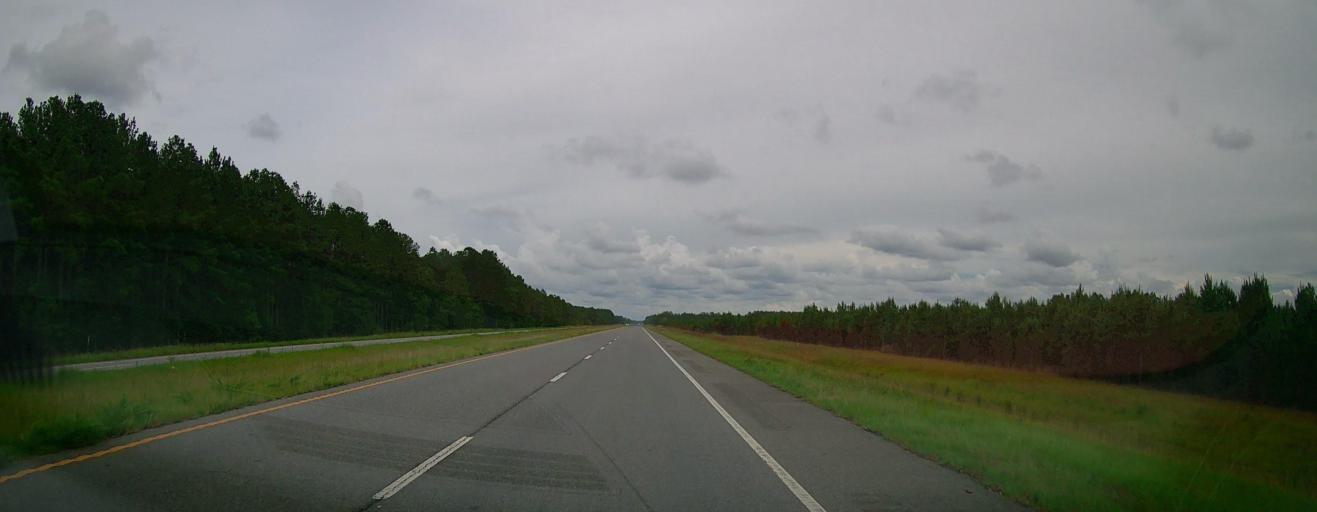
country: US
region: Georgia
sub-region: Appling County
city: Baxley
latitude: 31.7492
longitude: -82.2644
